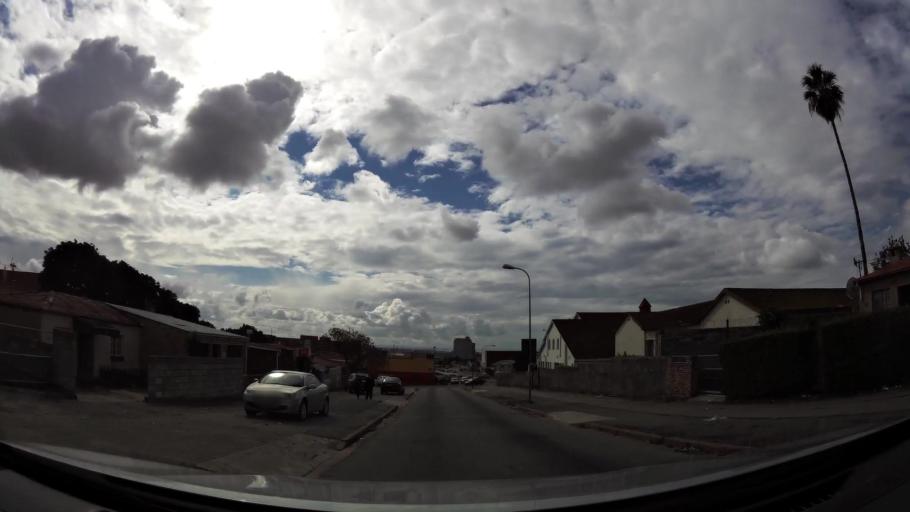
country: ZA
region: Eastern Cape
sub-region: Nelson Mandela Bay Metropolitan Municipality
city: Port Elizabeth
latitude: -33.9296
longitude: 25.5688
